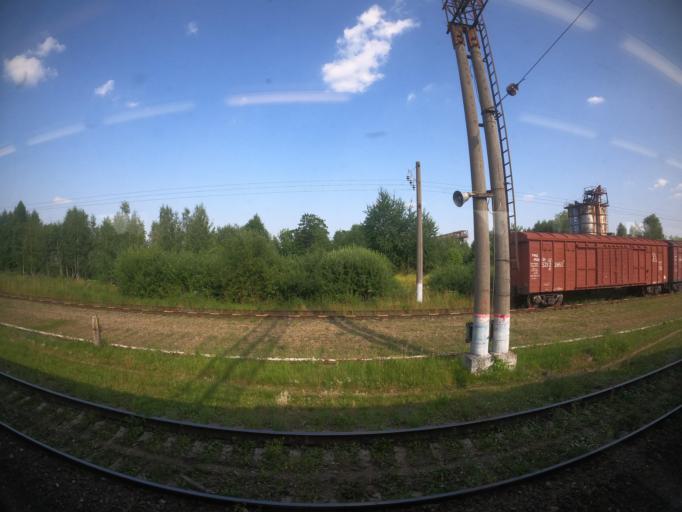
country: RU
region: Kaluga
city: Obninsk
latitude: 55.0983
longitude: 36.6211
